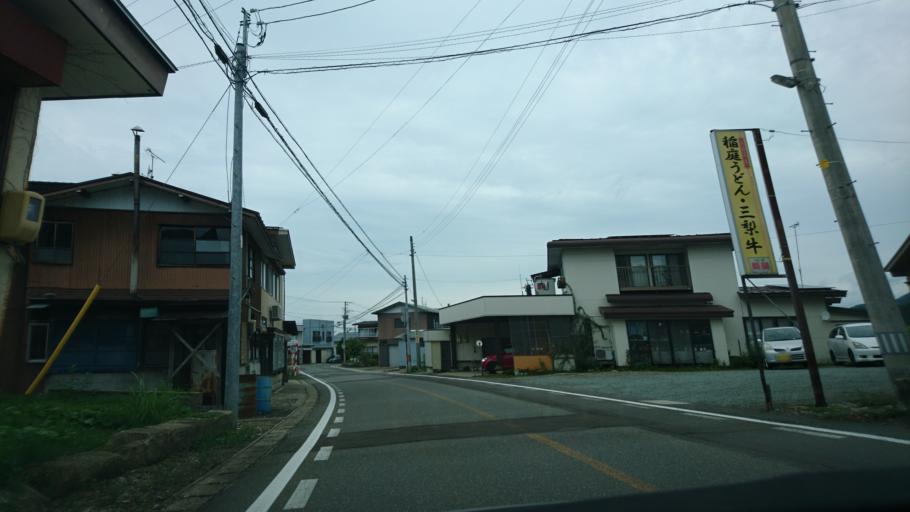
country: JP
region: Akita
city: Yuzawa
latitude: 39.1318
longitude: 140.5760
